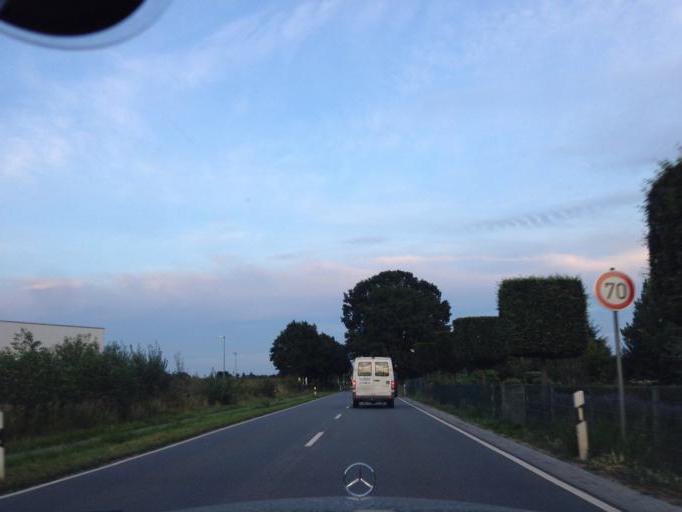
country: DE
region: Schleswig-Holstein
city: Hammoor
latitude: 53.7156
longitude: 10.2940
